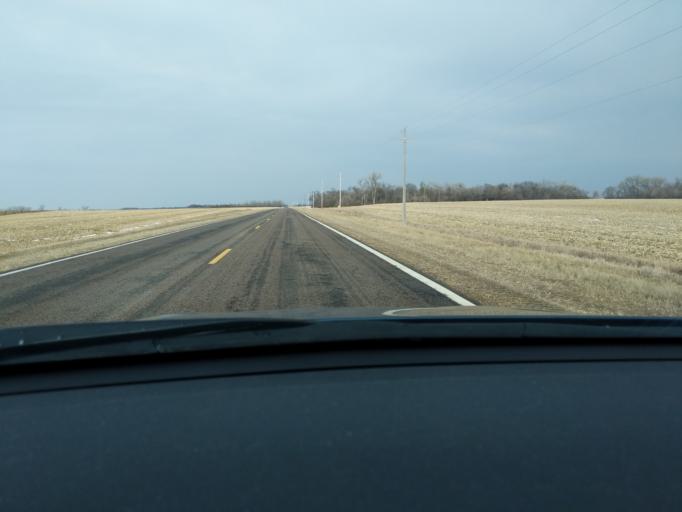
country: US
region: Minnesota
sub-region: Renville County
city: Renville
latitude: 44.7416
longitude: -95.3406
